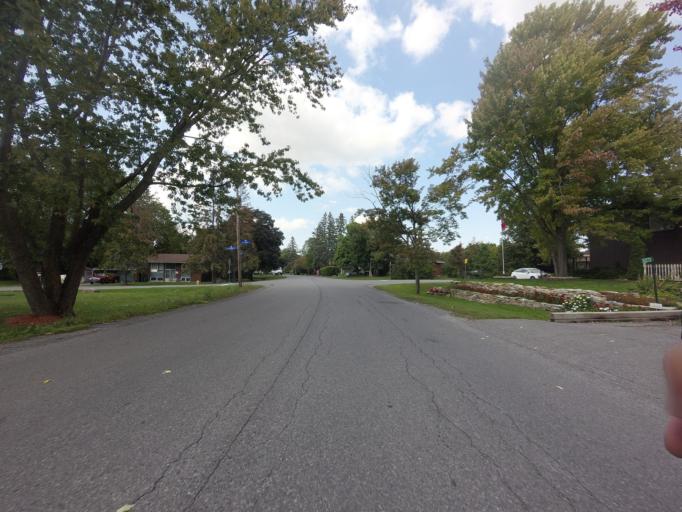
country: CA
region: Ontario
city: Bells Corners
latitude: 45.2397
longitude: -75.6991
